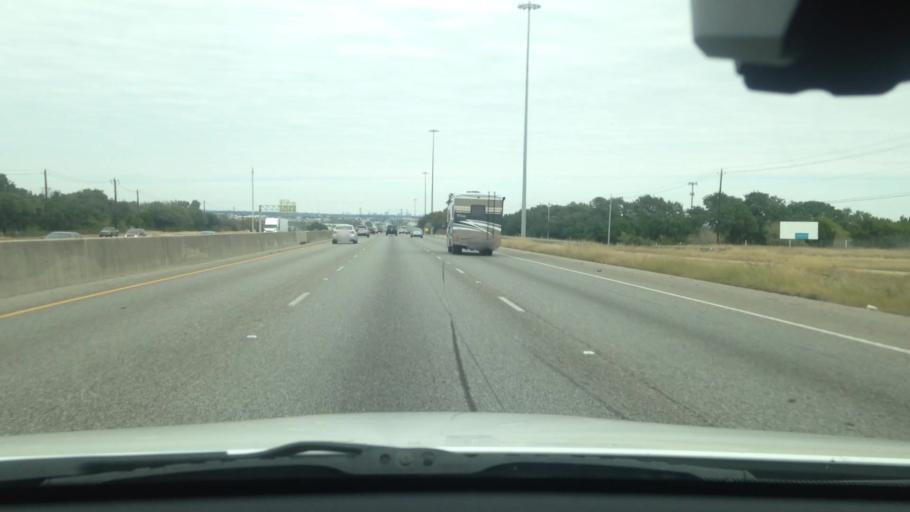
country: US
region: Texas
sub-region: Travis County
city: Onion Creek
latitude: 30.1232
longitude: -97.8025
